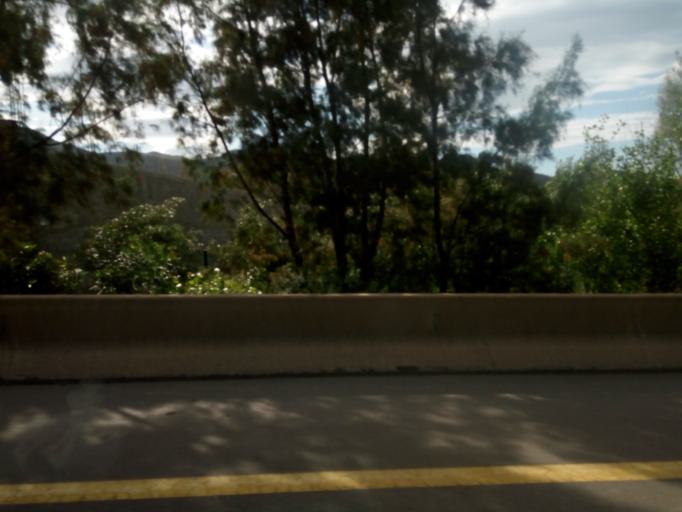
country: DZ
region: Tipaza
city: El Affroun
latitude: 36.4269
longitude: 2.5692
